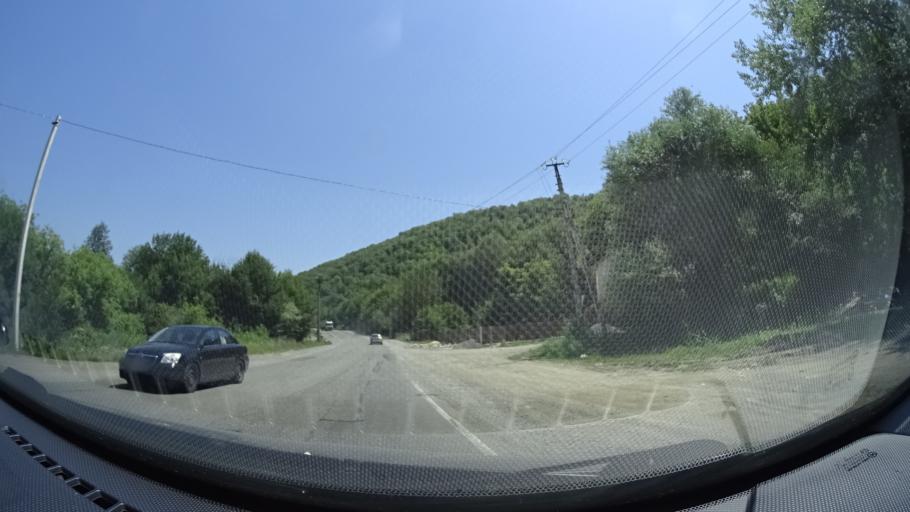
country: GE
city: Zhinvali
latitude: 42.1541
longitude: 44.7221
